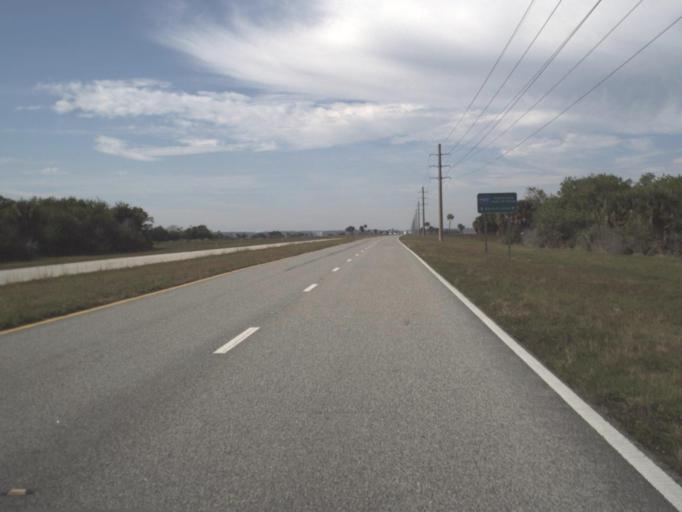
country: US
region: Florida
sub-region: Brevard County
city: Merritt Island
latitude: 28.5266
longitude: -80.7263
